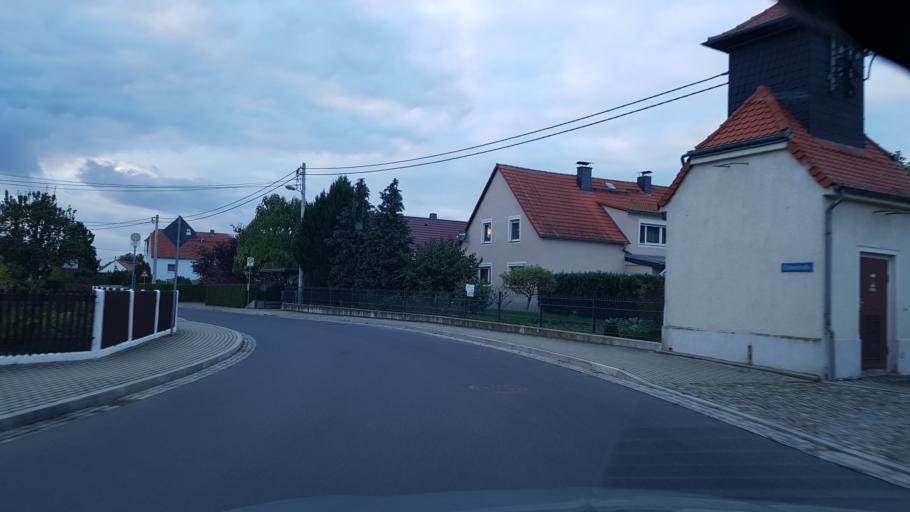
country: DE
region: Saxony
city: Grossenhain
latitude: 51.3195
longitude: 13.5839
